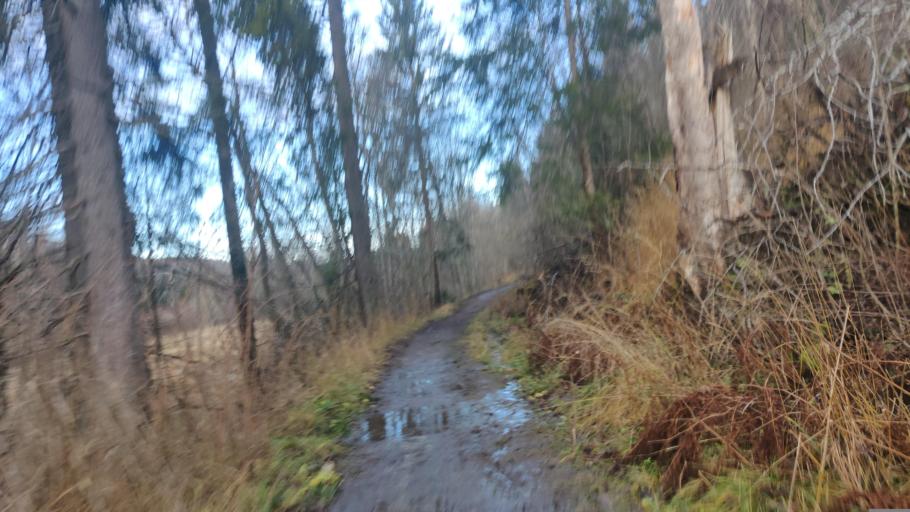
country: SE
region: Vaesternorrland
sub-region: Sundsvalls Kommun
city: Nolby
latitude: 62.3022
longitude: 17.3562
